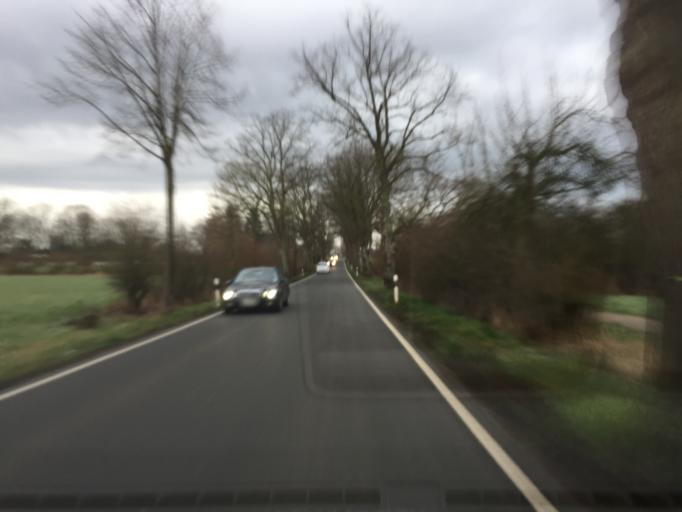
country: DE
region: Lower Saxony
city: Gross Munzel
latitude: 52.4220
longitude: 9.4976
